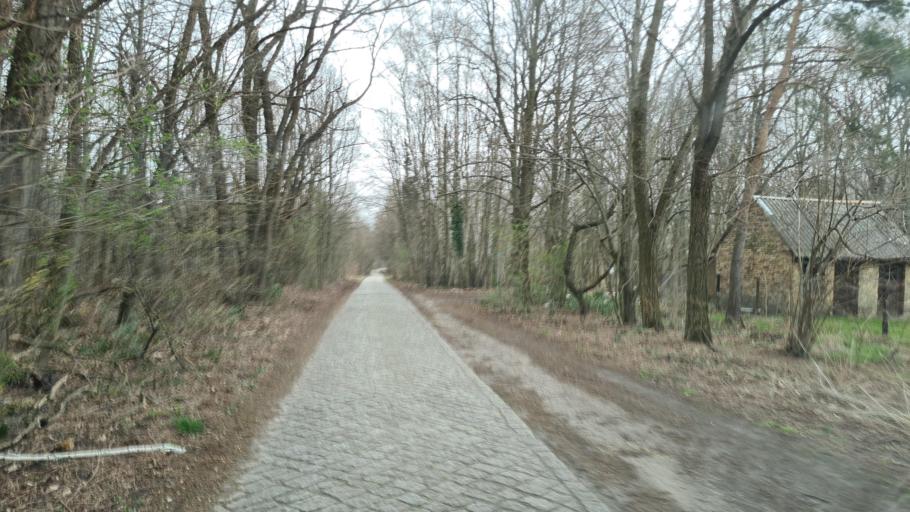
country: DE
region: Brandenburg
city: Schipkau
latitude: 51.5277
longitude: 13.8344
